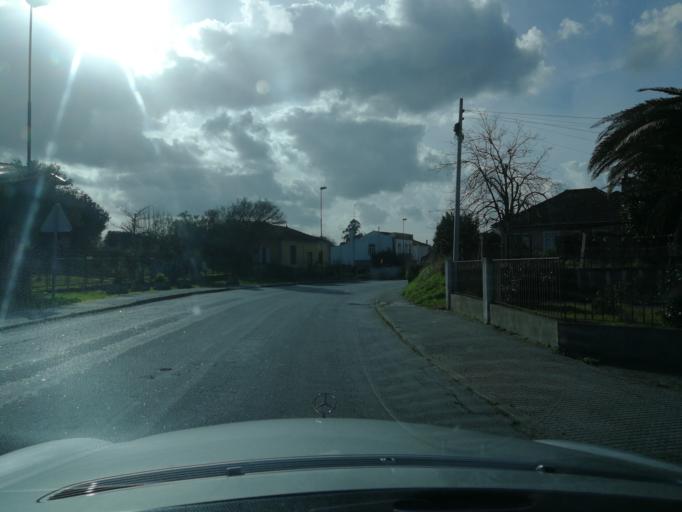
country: PT
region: Viana do Castelo
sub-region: Valenca
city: Valenza
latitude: 42.0285
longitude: -8.6333
